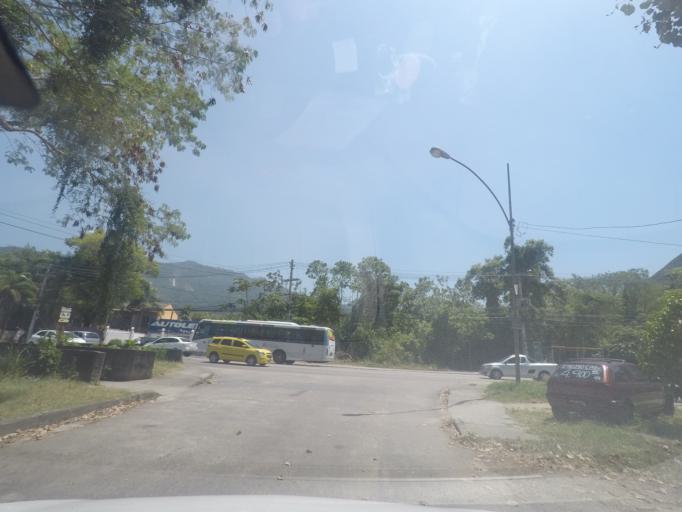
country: BR
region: Rio de Janeiro
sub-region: Nilopolis
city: Nilopolis
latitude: -22.9884
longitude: -43.4551
